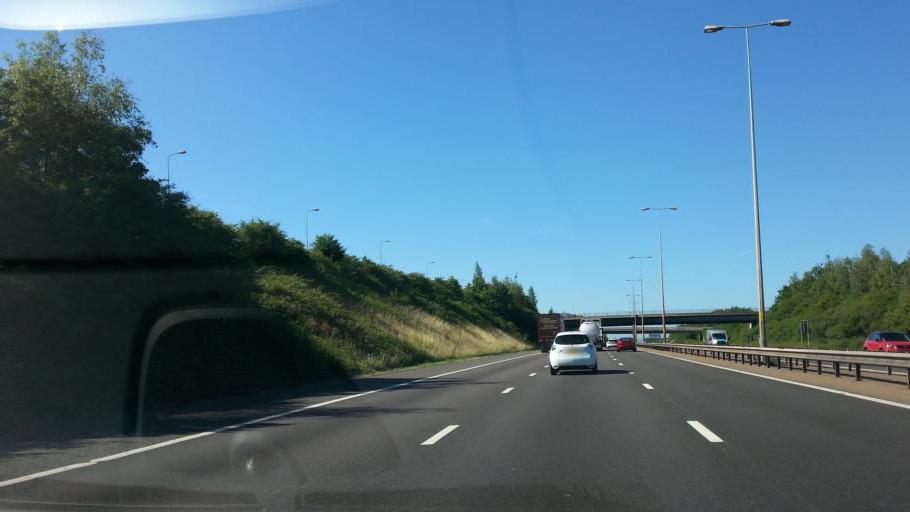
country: GB
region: England
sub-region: Worcestershire
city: Worcester
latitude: 52.1710
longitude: -2.1781
